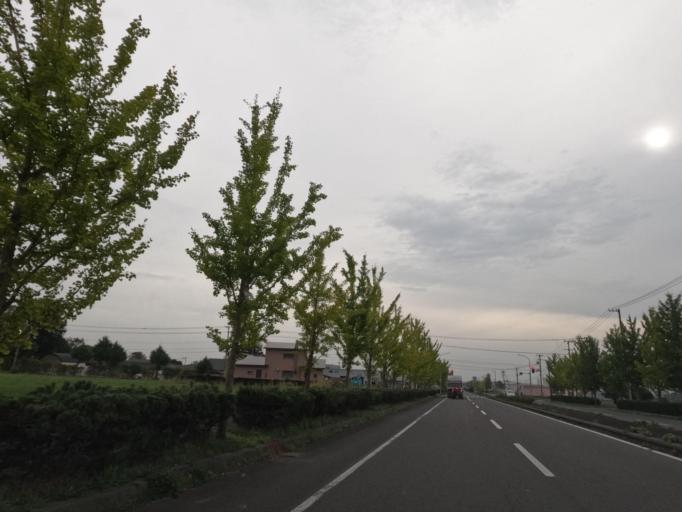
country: JP
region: Hokkaido
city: Date
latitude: 42.4766
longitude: 140.8853
